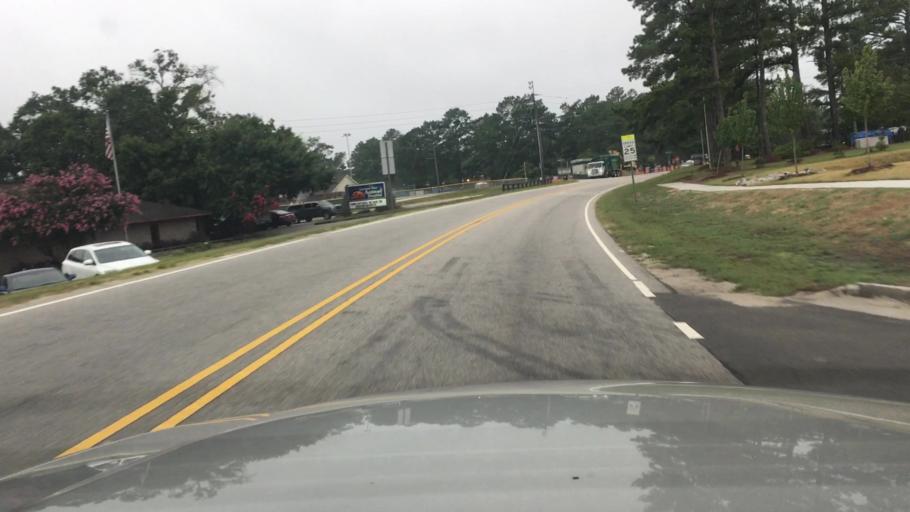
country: US
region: North Carolina
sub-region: Cumberland County
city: Hope Mills
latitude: 34.9730
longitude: -78.9539
